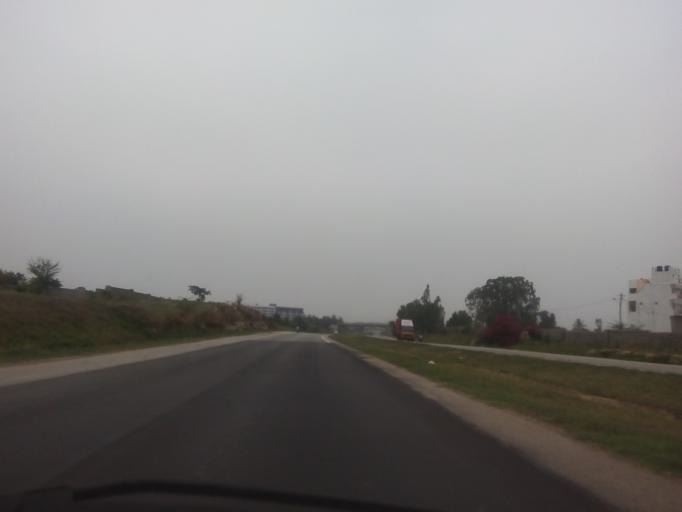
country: IN
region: Karnataka
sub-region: Bangalore Urban
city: Bangalore
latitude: 12.8603
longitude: 77.6196
